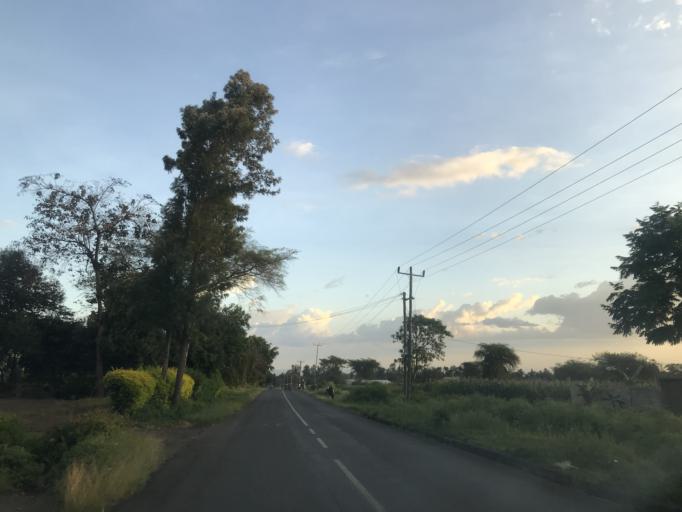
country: TZ
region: Arusha
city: Usa River
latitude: -3.3613
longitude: 36.8676
